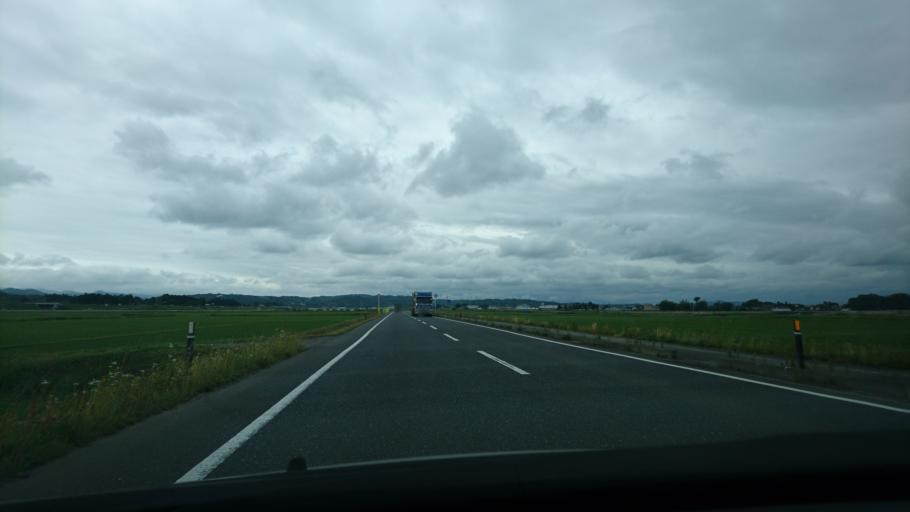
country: JP
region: Miyagi
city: Wakuya
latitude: 38.6826
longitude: 141.2611
